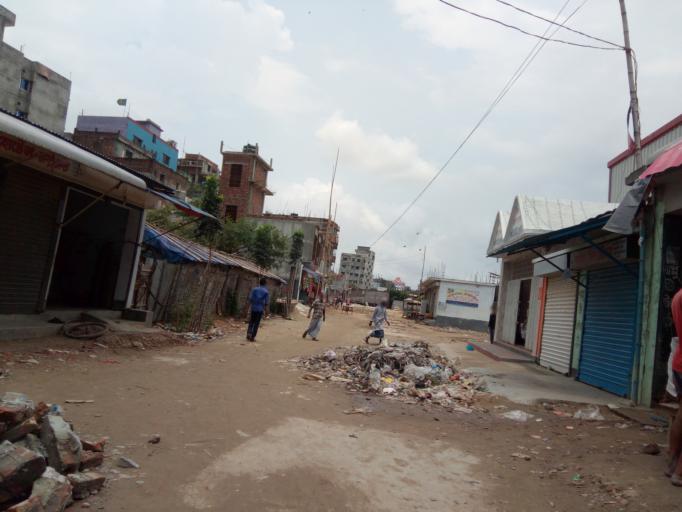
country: BD
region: Dhaka
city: Azimpur
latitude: 23.7286
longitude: 90.3686
